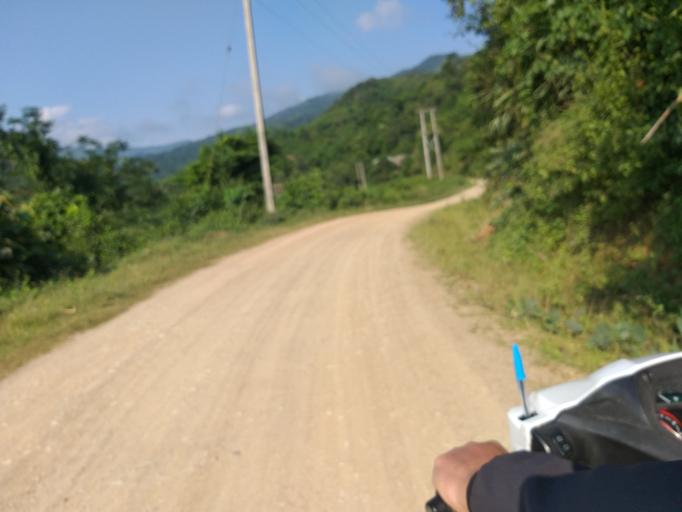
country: LA
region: Phongsali
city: Khoa
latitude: 21.2004
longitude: 102.6824
